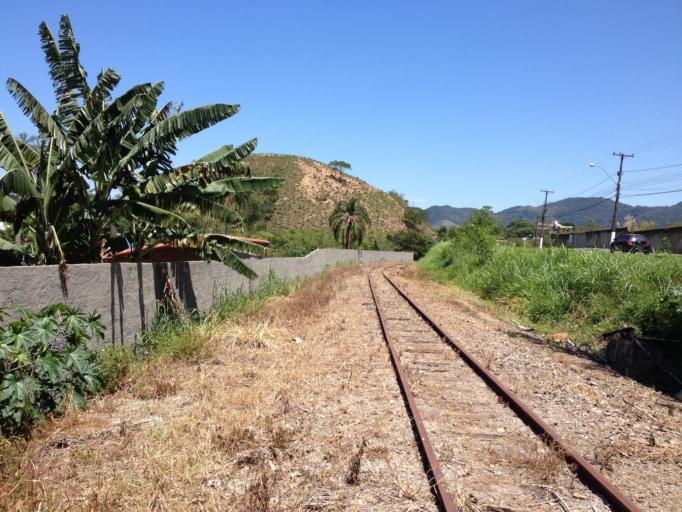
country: BR
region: Rio de Janeiro
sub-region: Rio Bonito
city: Rio Bonito
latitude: -22.7102
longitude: -42.6388
